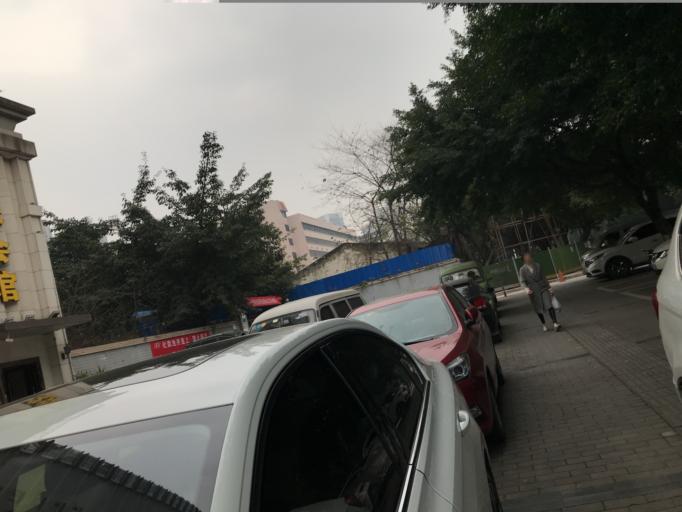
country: CN
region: Chongqing Shi
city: Chongqing
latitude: 29.5259
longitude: 106.5457
